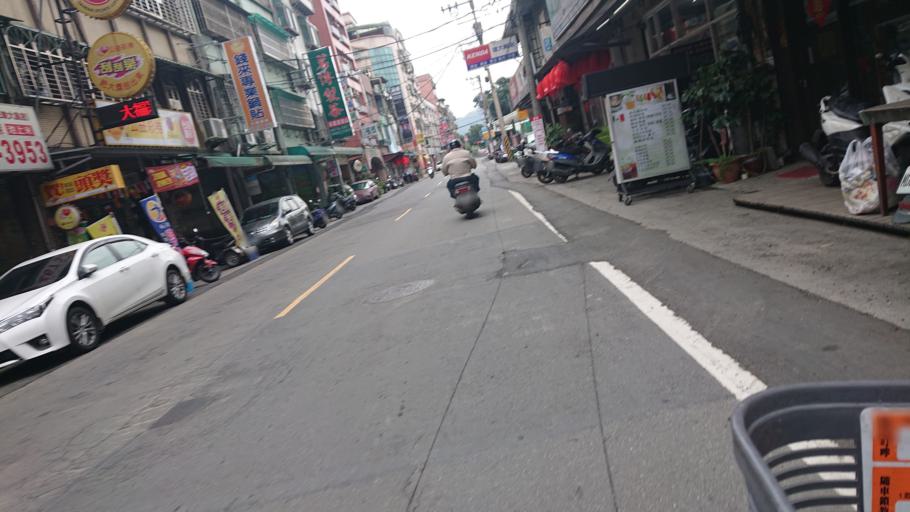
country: TW
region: Taiwan
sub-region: Taoyuan
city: Taoyuan
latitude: 24.9368
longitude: 121.3672
